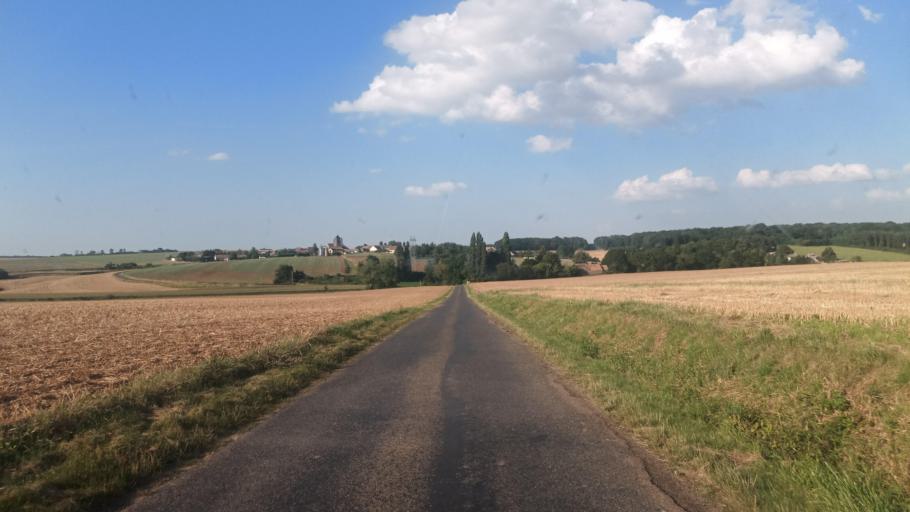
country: FR
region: Bourgogne
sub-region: Departement de l'Yonne
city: Saint-Valerien
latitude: 48.2308
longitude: 3.0909
